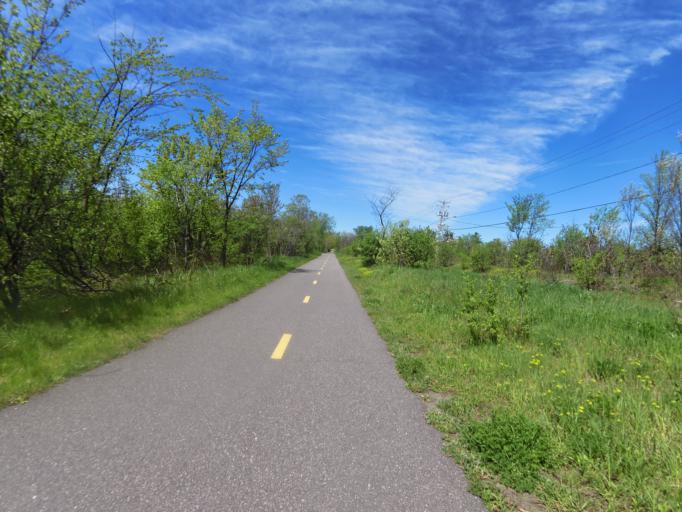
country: CA
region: Ontario
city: Bells Corners
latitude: 45.3861
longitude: -75.8310
